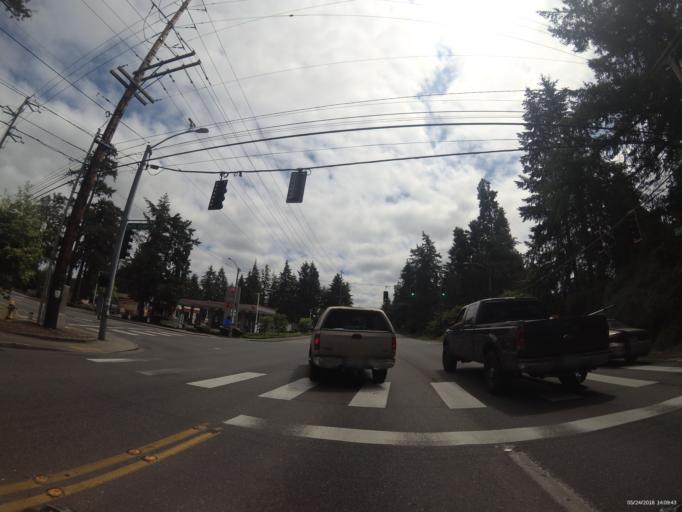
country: US
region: Washington
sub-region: Pierce County
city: Lakewood
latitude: 47.1393
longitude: -122.5261
